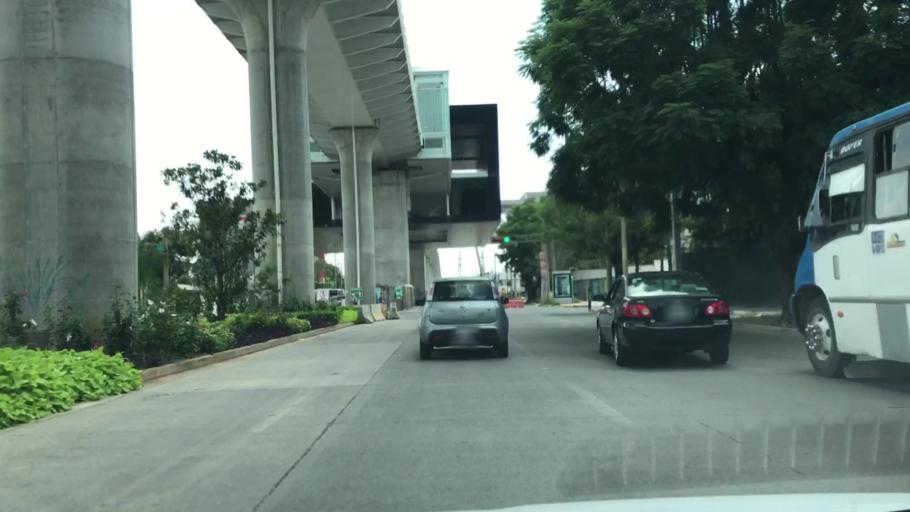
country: MX
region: Jalisco
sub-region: Zapopan
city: Zapopan
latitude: 20.7072
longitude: -103.3672
